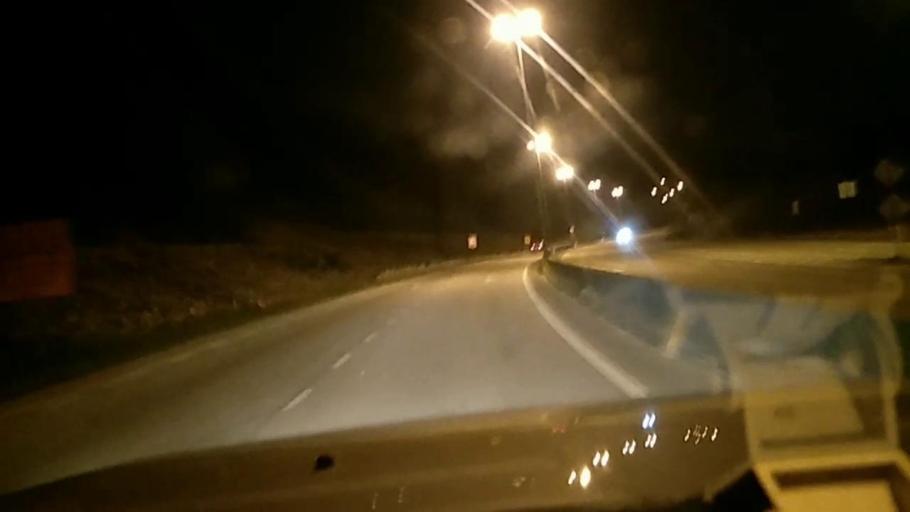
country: MY
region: Selangor
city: Kampung Baru Subang
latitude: 3.1327
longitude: 101.5030
